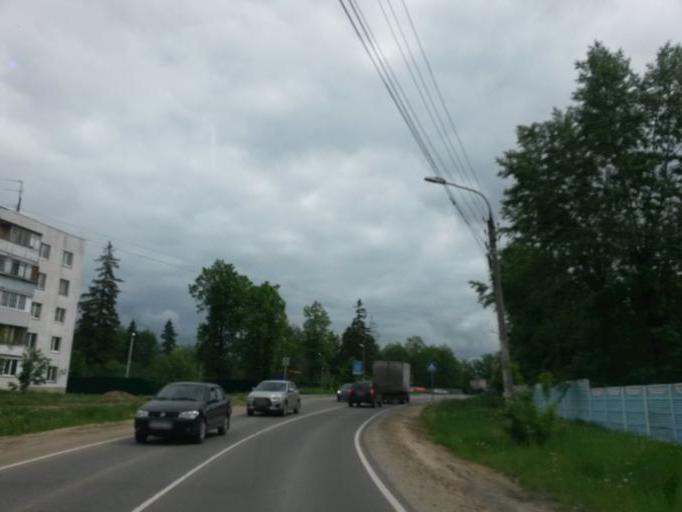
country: RU
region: Moskovskaya
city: Klimovsk
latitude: 55.3470
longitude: 37.5546
